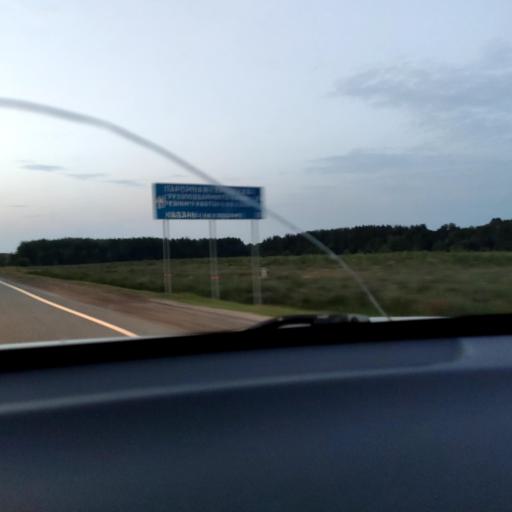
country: RU
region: Tatarstan
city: Verkhniy Uslon
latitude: 55.6613
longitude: 48.8588
